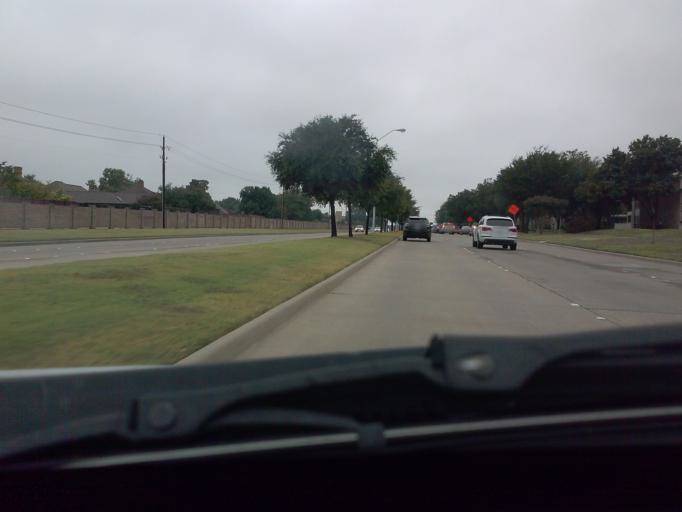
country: US
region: Texas
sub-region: Collin County
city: Plano
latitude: 33.0574
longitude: -96.7425
